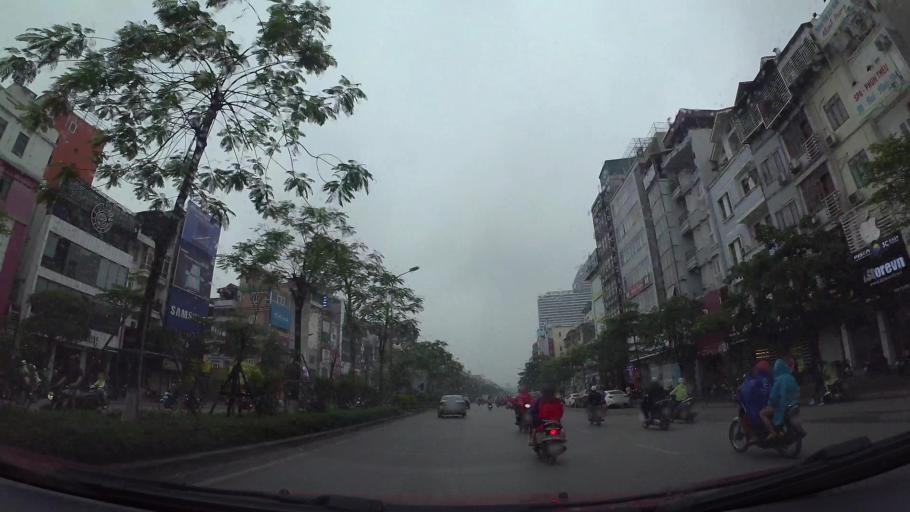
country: VN
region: Ha Noi
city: Dong Da
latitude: 21.0166
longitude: 105.8317
